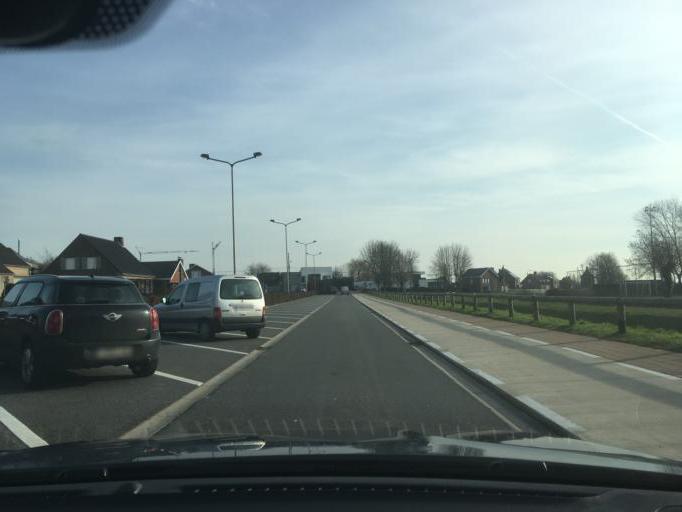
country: BE
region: Flanders
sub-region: Provincie West-Vlaanderen
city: Meulebeke
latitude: 50.9449
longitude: 3.2813
